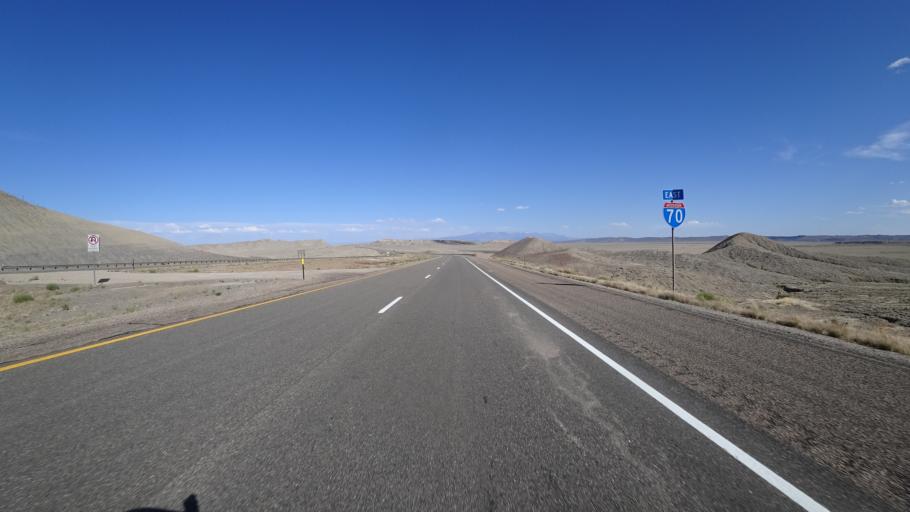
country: US
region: Utah
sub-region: Grand County
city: Moab
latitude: 38.9593
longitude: -109.7123
